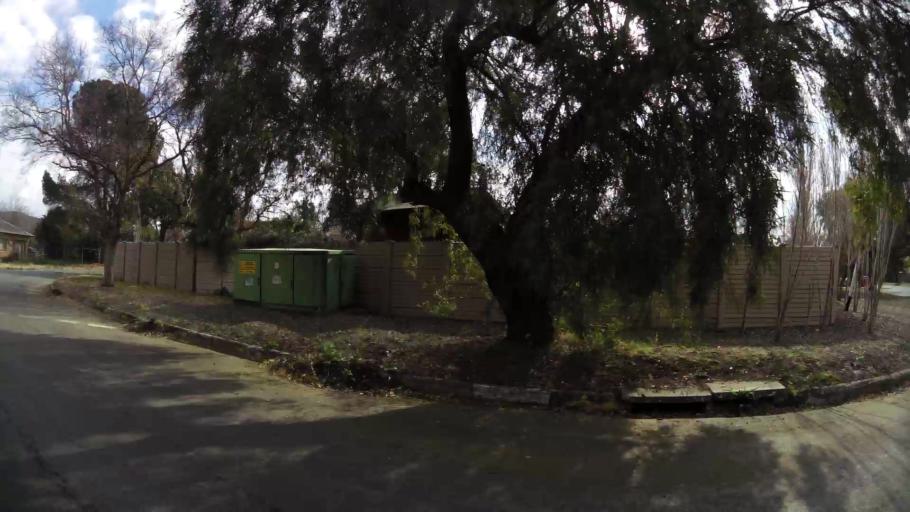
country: ZA
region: Orange Free State
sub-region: Mangaung Metropolitan Municipality
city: Bloemfontein
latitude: -29.0906
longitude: 26.2508
